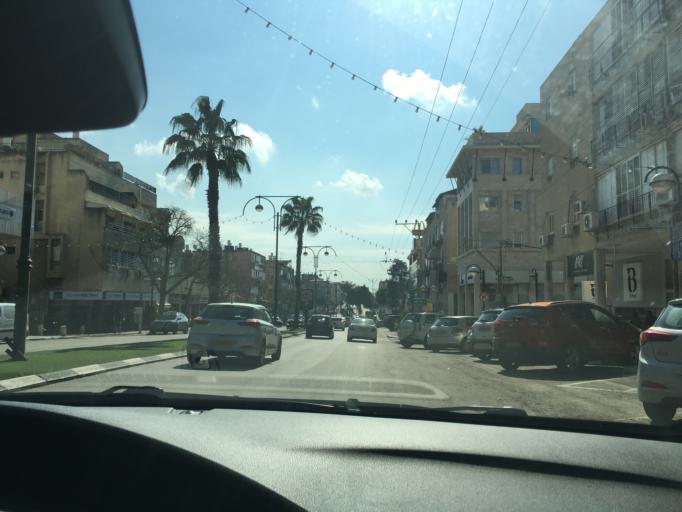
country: IL
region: Tel Aviv
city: Ramat HaSharon
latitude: 32.1485
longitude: 34.8397
